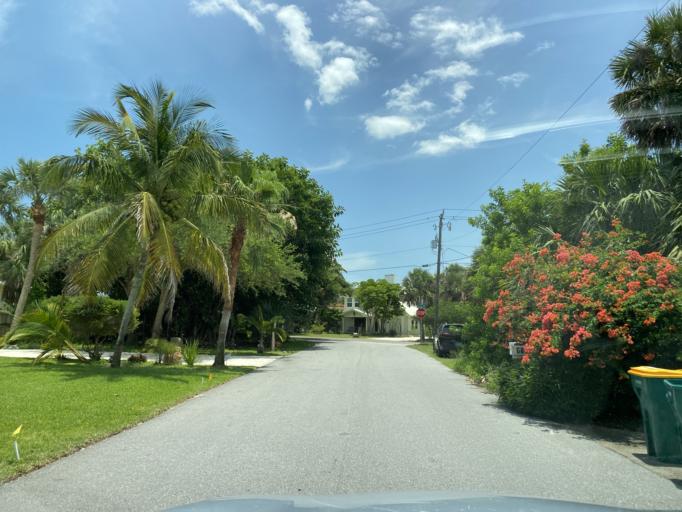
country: US
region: Florida
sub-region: Brevard County
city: Micco
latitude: 27.9396
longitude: -80.4943
